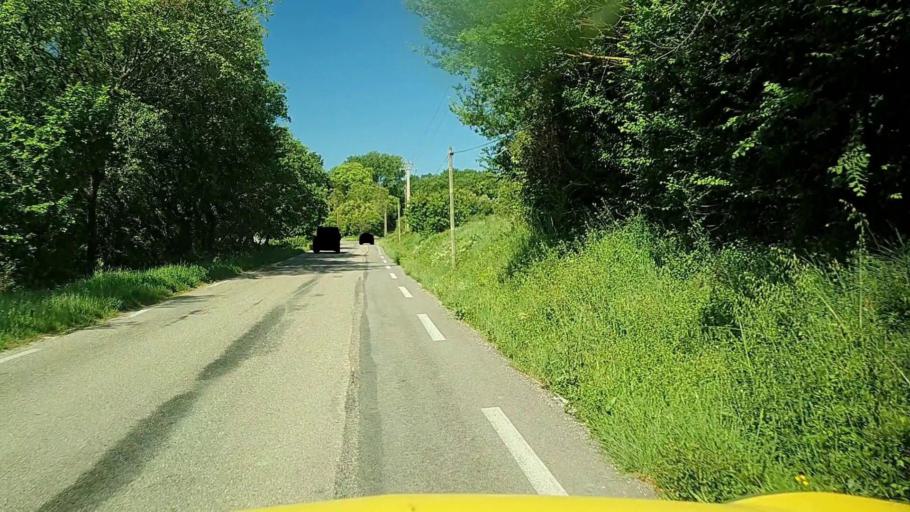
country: FR
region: Languedoc-Roussillon
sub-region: Departement du Gard
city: Blauzac
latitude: 43.9458
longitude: 4.3710
